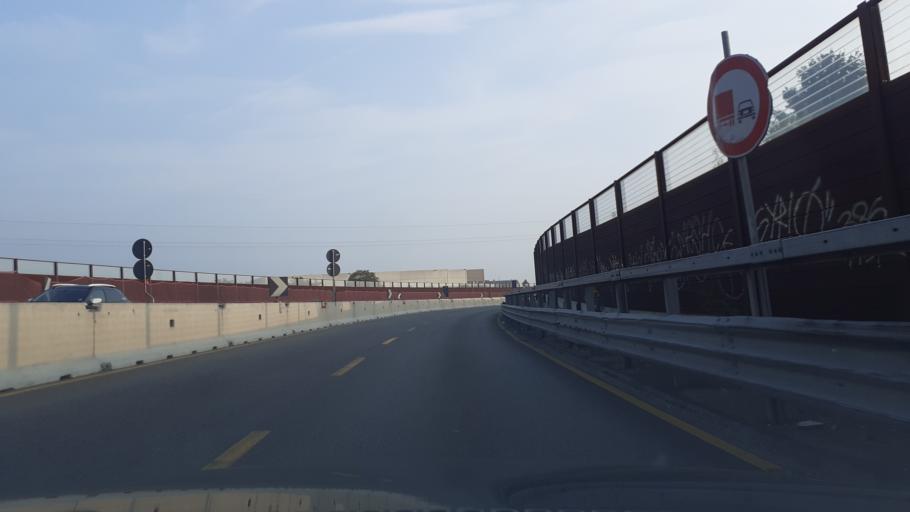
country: IT
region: Lombardy
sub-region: Citta metropolitana di Milano
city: Paderno Dugnano
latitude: 45.5555
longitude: 9.1456
